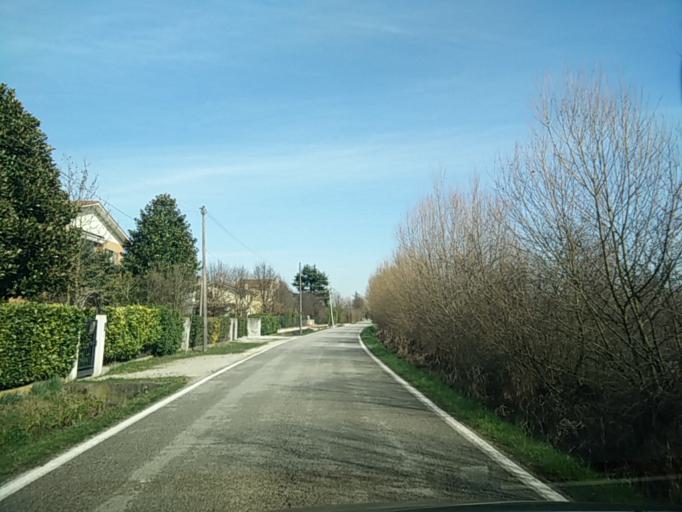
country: IT
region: Veneto
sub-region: Provincia di Treviso
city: San Floriano-Olmi
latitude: 45.6573
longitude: 12.3363
